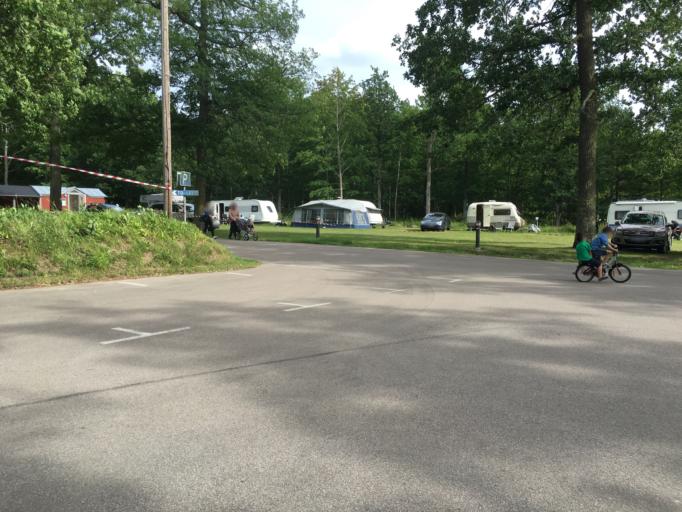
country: SE
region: Kalmar
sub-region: Nybro Kommun
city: Nybro
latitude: 56.9399
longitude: 15.9074
